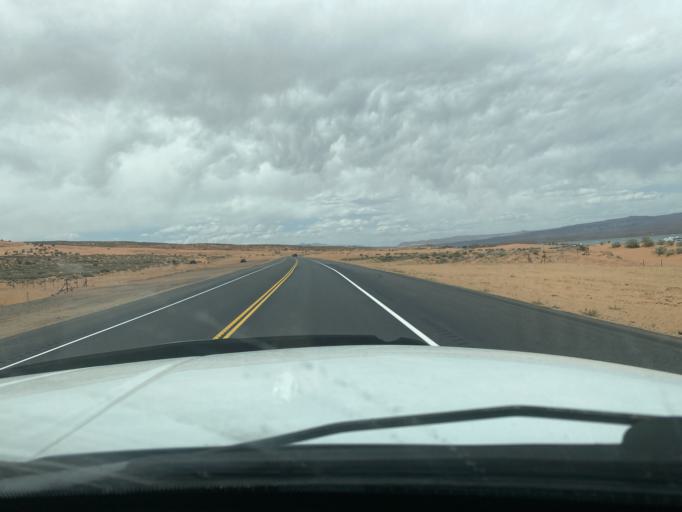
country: US
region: Utah
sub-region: Washington County
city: Hurricane
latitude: 37.0985
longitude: -113.3703
